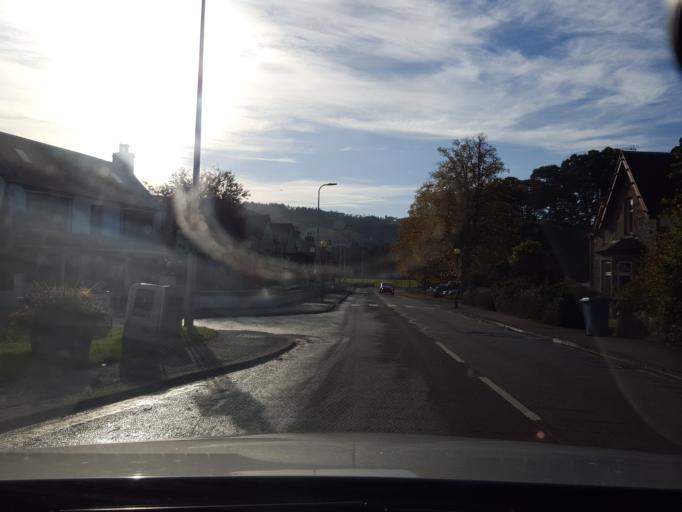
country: GB
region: Scotland
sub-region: Highland
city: Beauly
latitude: 57.3358
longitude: -4.4800
